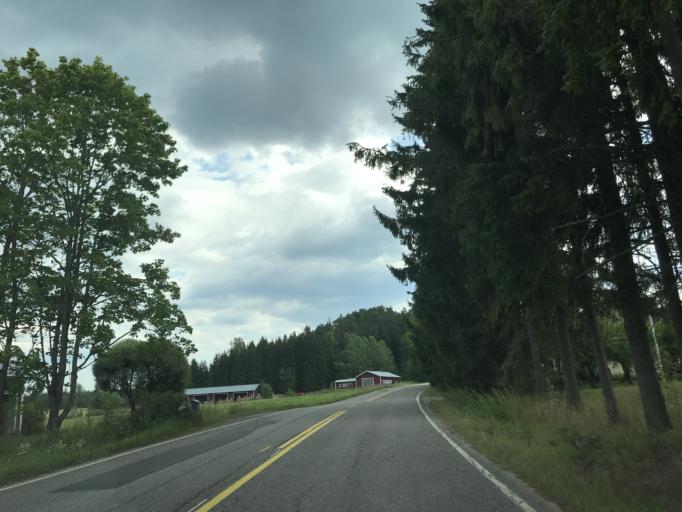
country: FI
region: Uusimaa
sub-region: Helsinki
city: Vihti
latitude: 60.3861
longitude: 24.3500
